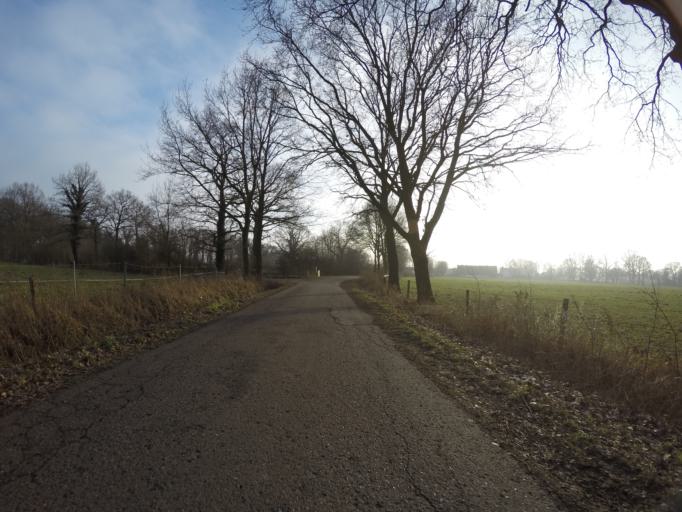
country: DE
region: Schleswig-Holstein
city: Quickborn
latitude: 53.7162
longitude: 9.8956
